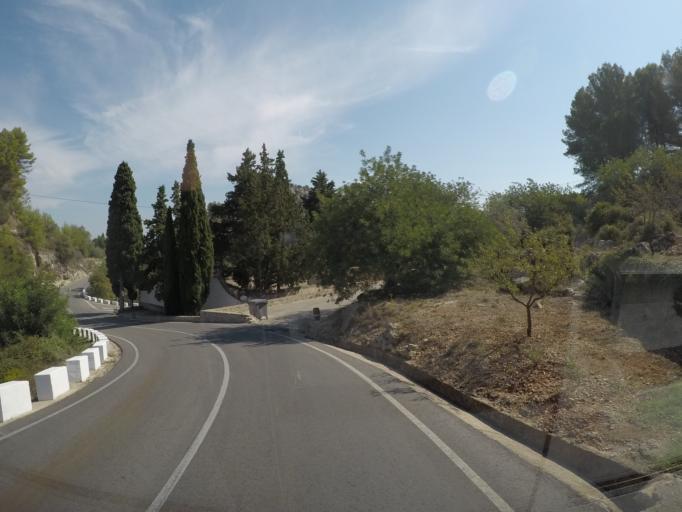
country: ES
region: Valencia
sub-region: Provincia de Alicante
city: Murla
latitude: 38.7800
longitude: -0.0963
